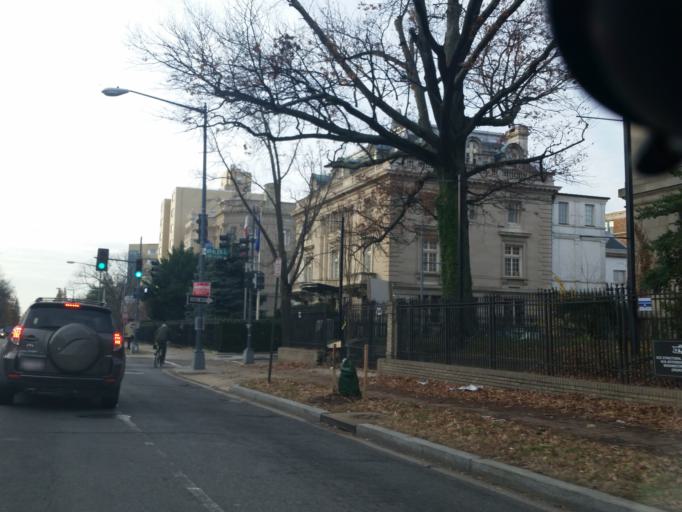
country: US
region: Washington, D.C.
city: Washington, D.C.
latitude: 38.9251
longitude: -77.0365
